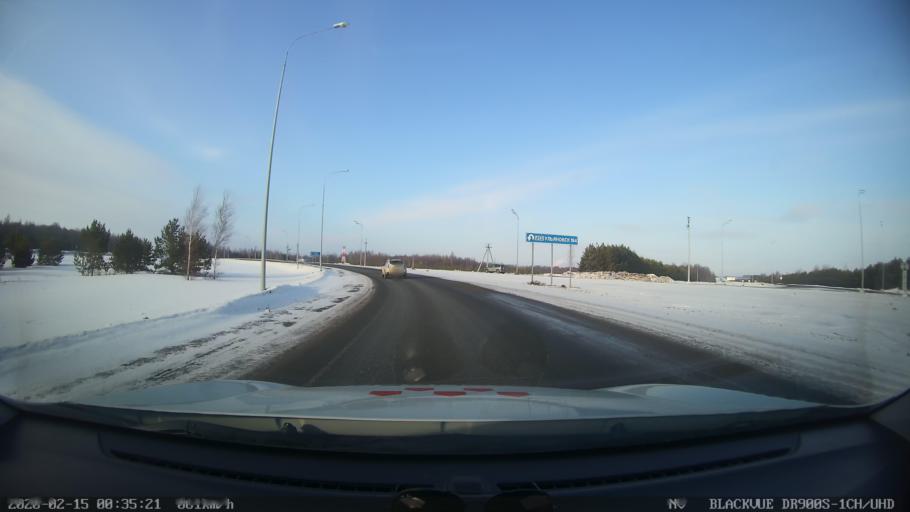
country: RU
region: Tatarstan
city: Verkhniy Uslon
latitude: 55.7073
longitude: 48.8924
